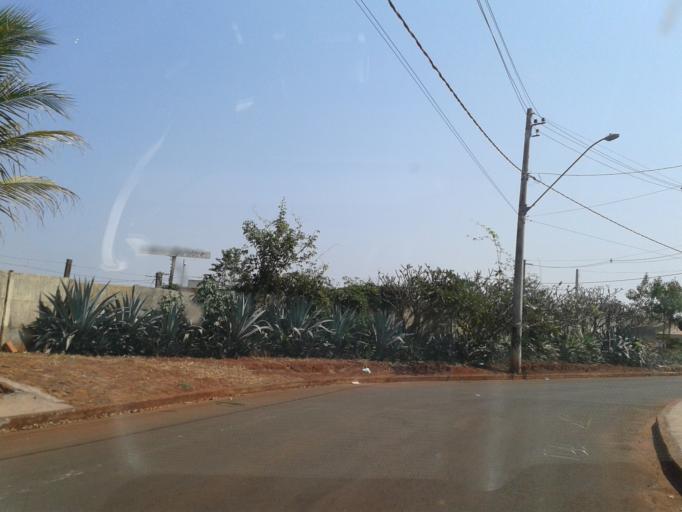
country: BR
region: Minas Gerais
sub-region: Ituiutaba
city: Ituiutaba
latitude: -18.9790
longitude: -49.4827
